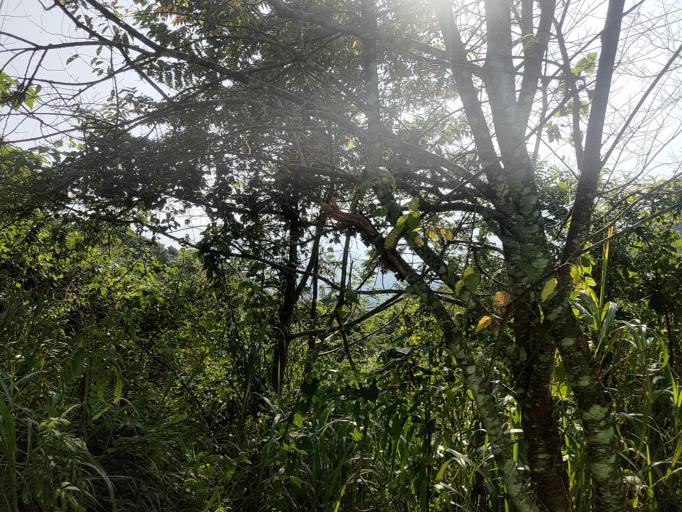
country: TW
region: Taiwan
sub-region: Hsinchu
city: Hsinchu
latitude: 24.6147
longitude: 121.0920
